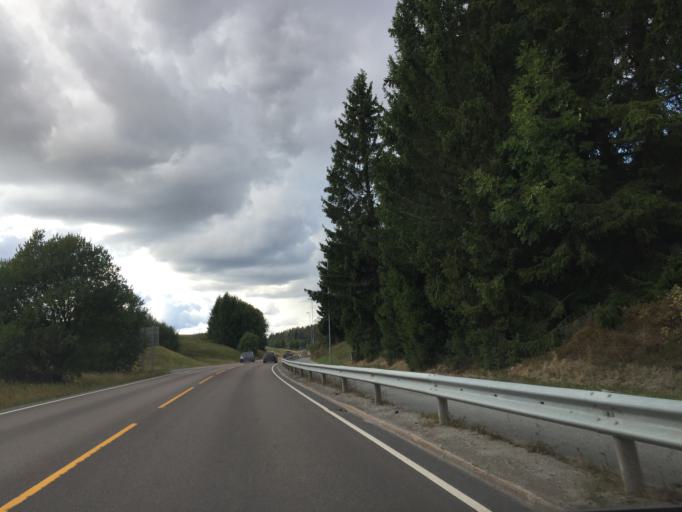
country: NO
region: Ostfold
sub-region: Askim
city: Askim
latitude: 59.5852
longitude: 11.1297
